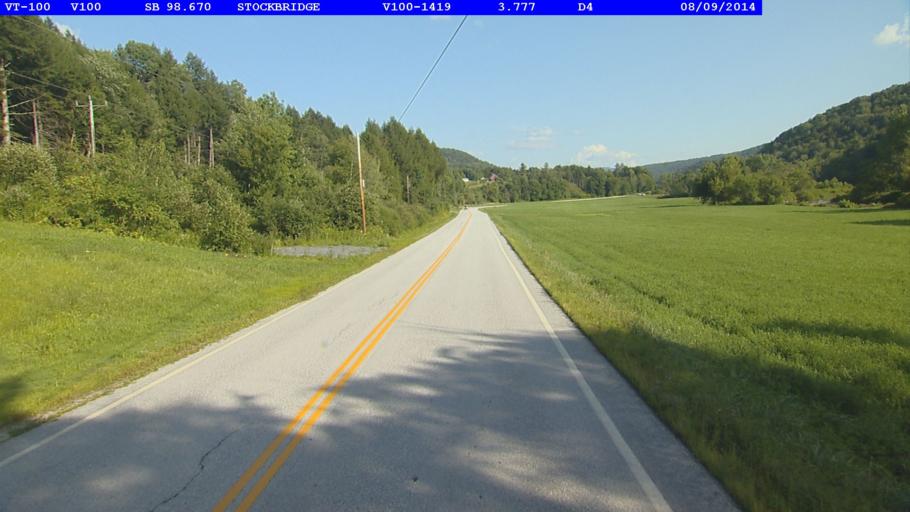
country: US
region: Vermont
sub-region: Orange County
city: Randolph
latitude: 43.7926
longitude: -72.7639
